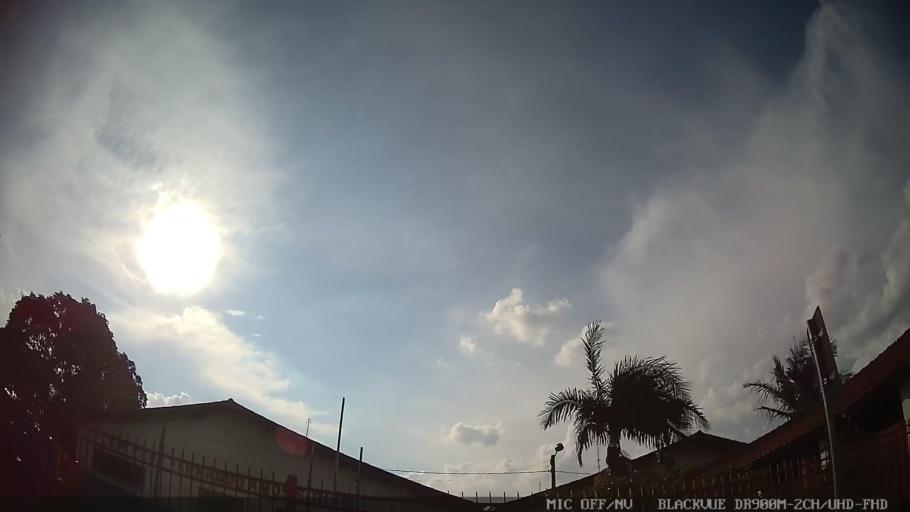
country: BR
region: Sao Paulo
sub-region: Braganca Paulista
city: Braganca Paulista
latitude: -22.9192
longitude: -46.5454
